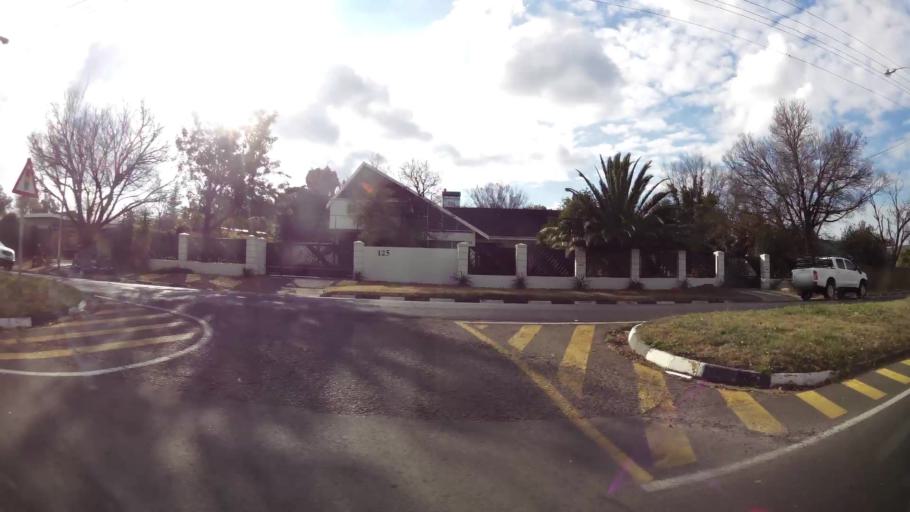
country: ZA
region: Orange Free State
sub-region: Mangaung Metropolitan Municipality
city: Bloemfontein
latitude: -29.0806
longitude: 26.2087
